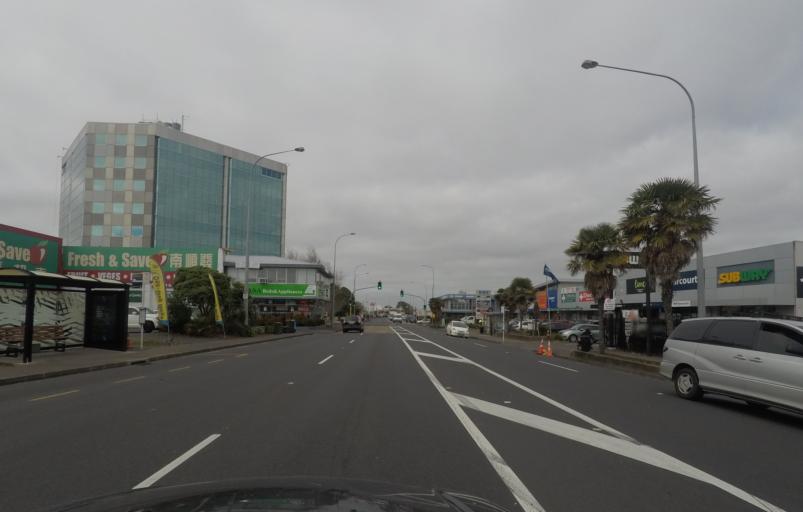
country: NZ
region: Auckland
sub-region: Auckland
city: Mangere
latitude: -36.9461
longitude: 174.8453
